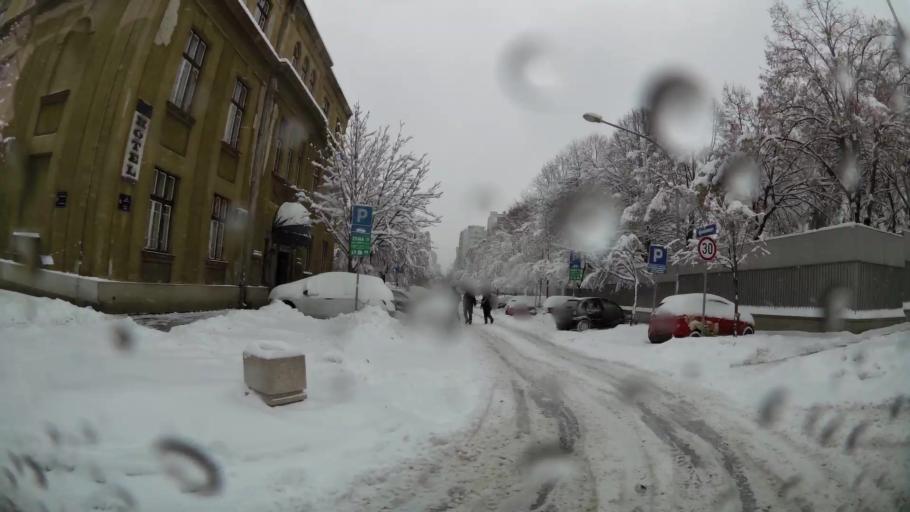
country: RS
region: Central Serbia
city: Belgrade
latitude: 44.8000
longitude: 20.4614
